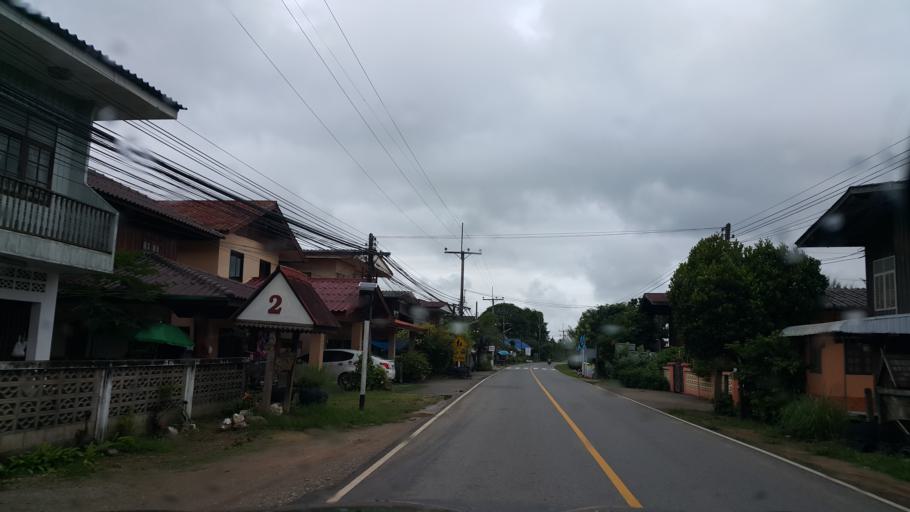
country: TH
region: Phayao
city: Chiang Kham
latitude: 19.5248
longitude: 100.3307
